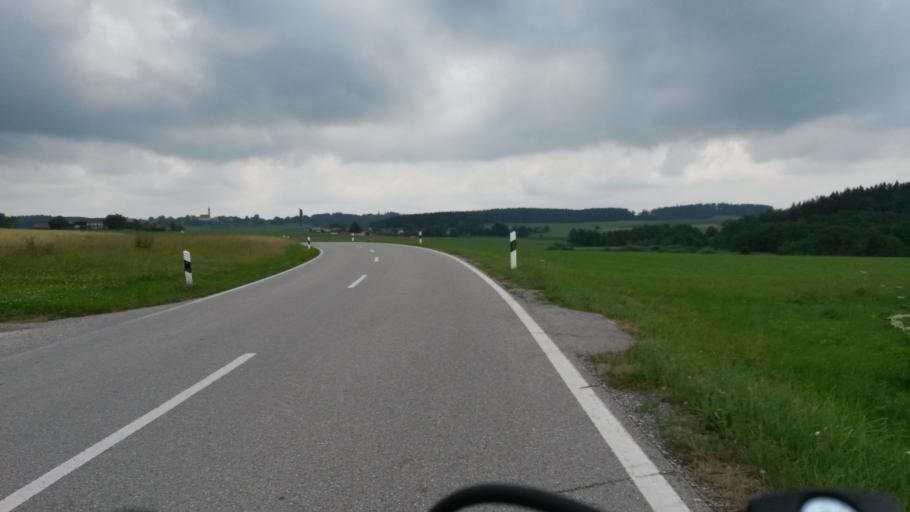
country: DE
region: Bavaria
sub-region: Upper Bavaria
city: Hoslwang
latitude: 47.9350
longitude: 12.3438
